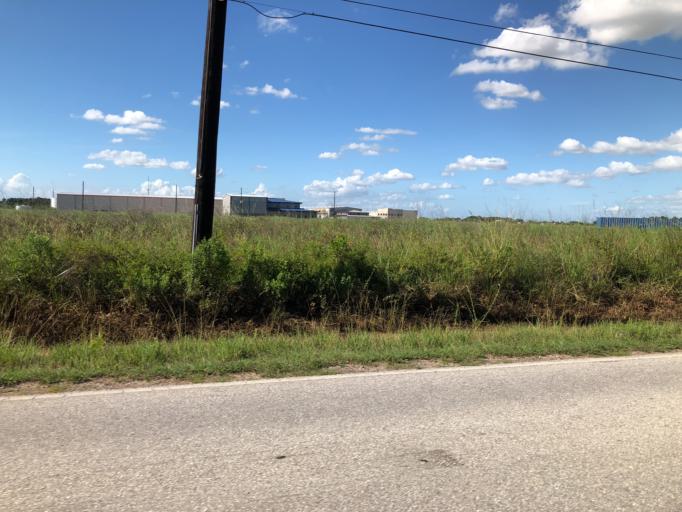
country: US
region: Texas
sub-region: Harris County
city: Katy
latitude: 29.8313
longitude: -95.8142
